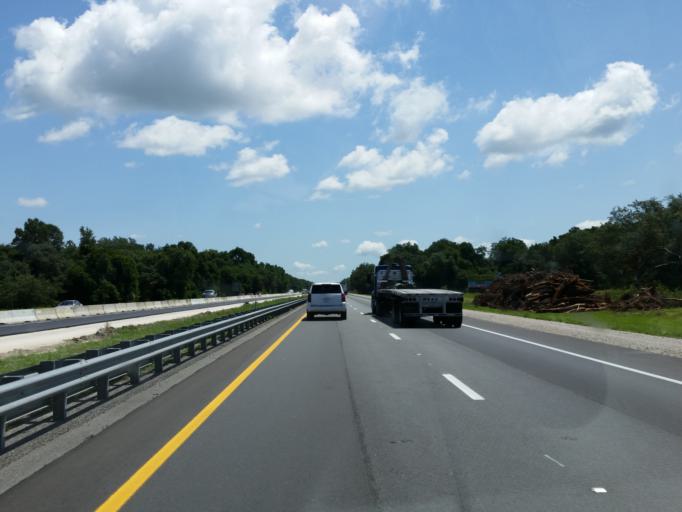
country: US
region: Florida
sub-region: Sumter County
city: Bushnell
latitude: 28.6133
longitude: -82.1921
